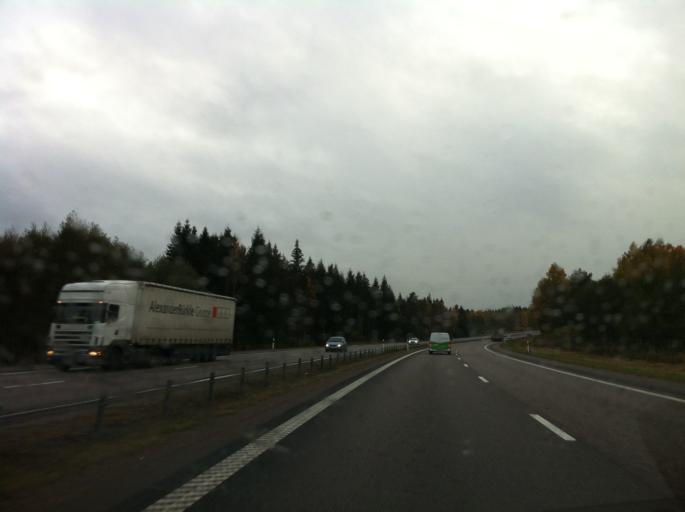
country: SE
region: OEstergoetland
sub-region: Odeshogs Kommun
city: OEdeshoeg
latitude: 58.2191
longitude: 14.6497
